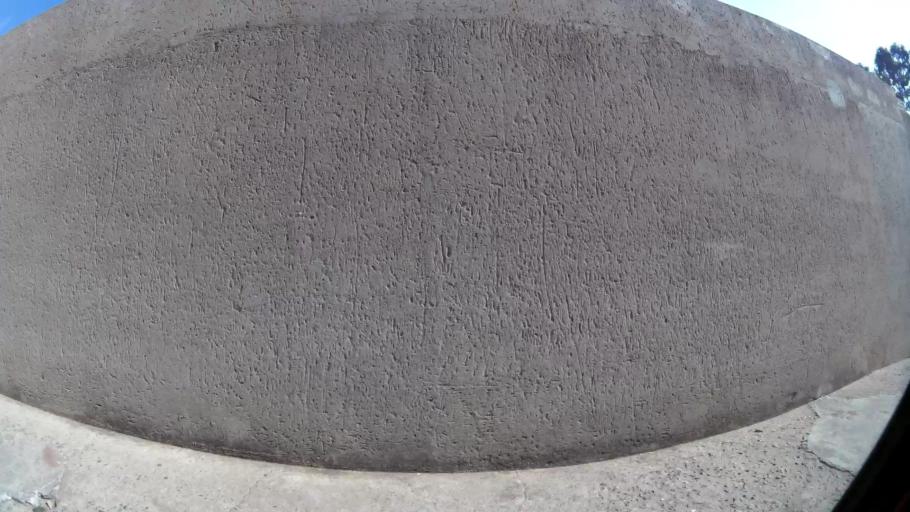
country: ZA
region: Gauteng
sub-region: City of Johannesburg Metropolitan Municipality
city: Soweto
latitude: -26.2417
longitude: 27.9440
